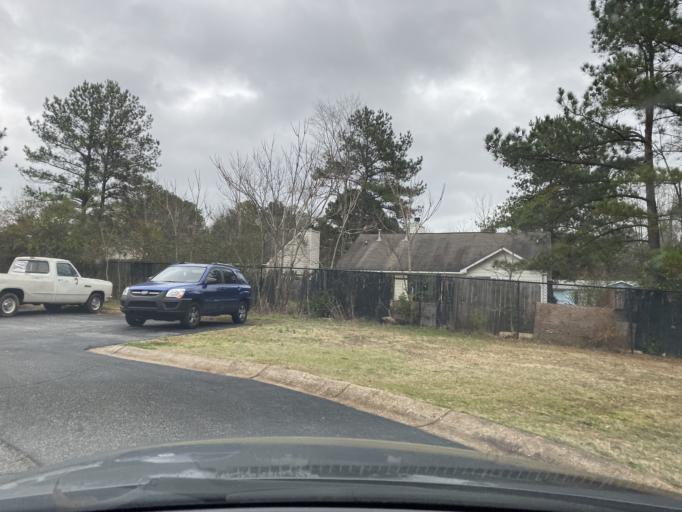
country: US
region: Georgia
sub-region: DeKalb County
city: Pine Mountain
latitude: 33.6992
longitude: -84.1441
